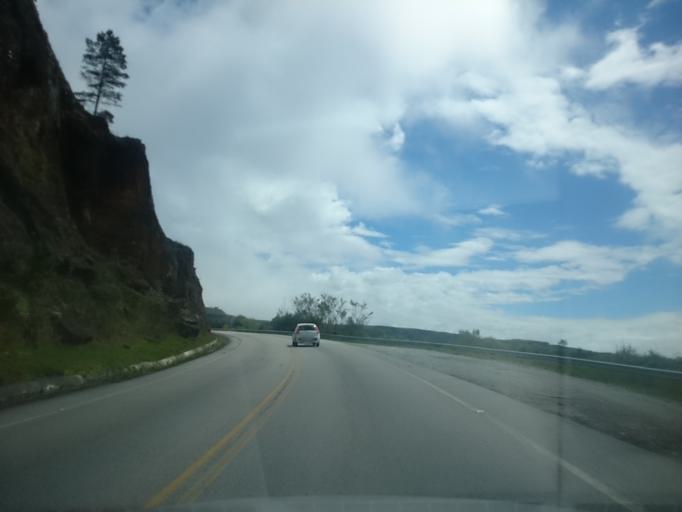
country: BR
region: Santa Catarina
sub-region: Anitapolis
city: Anitapolis
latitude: -27.6903
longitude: -49.1267
